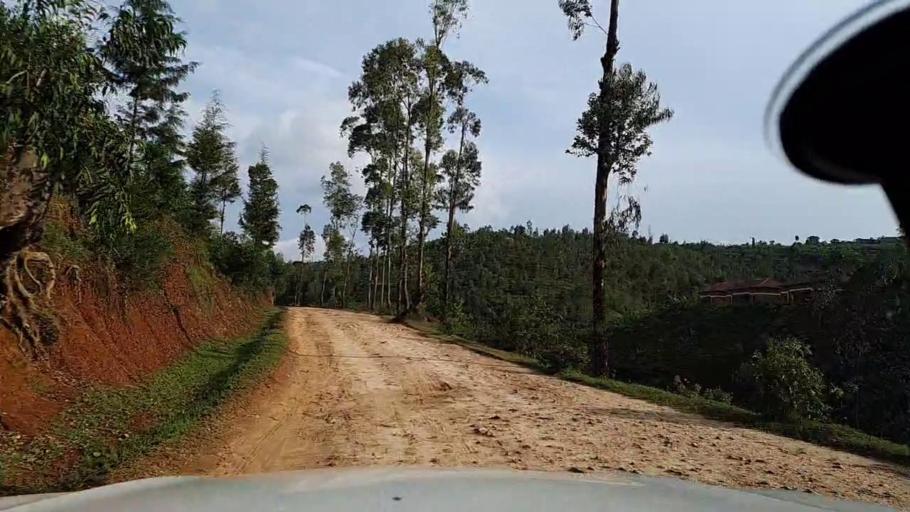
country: RW
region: Southern Province
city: Gitarama
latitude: -2.1740
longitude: 29.5555
